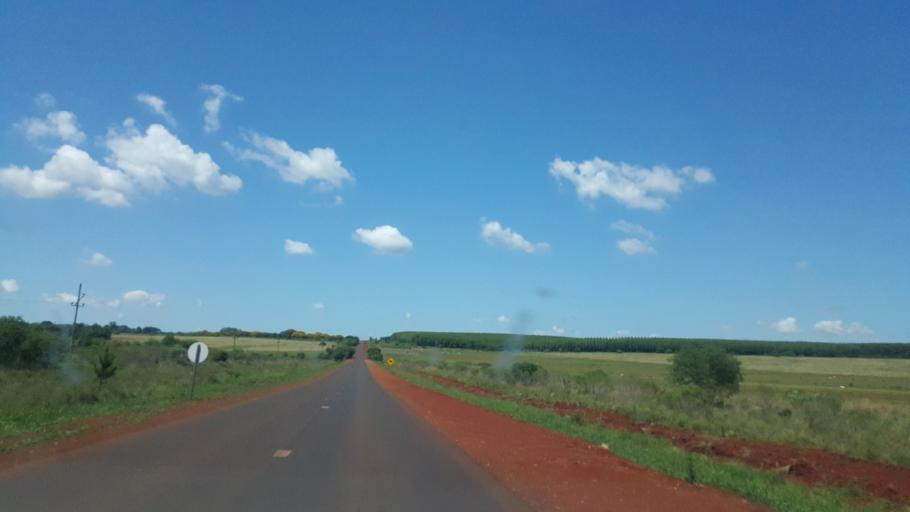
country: AR
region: Corrientes
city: Santo Tome
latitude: -28.3404
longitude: -55.9282
